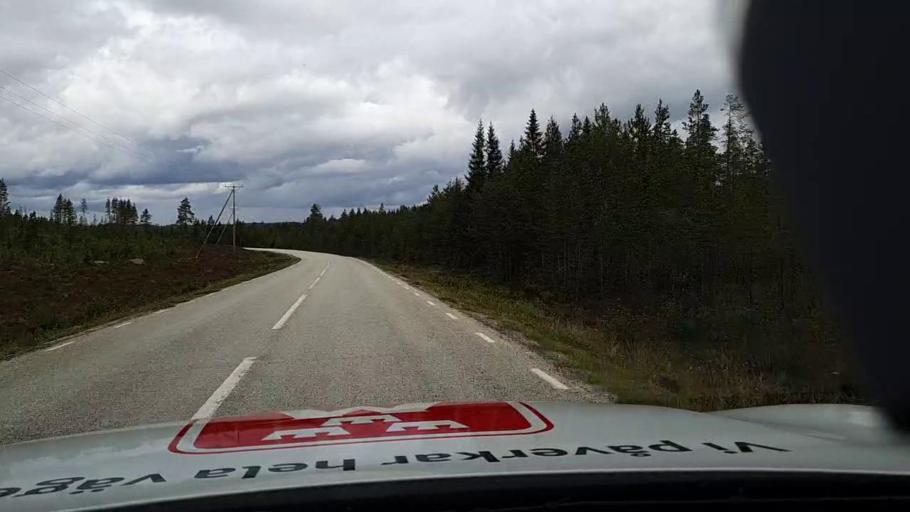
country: SE
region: Jaemtland
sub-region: Are Kommun
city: Jarpen
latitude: 62.8071
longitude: 13.6590
